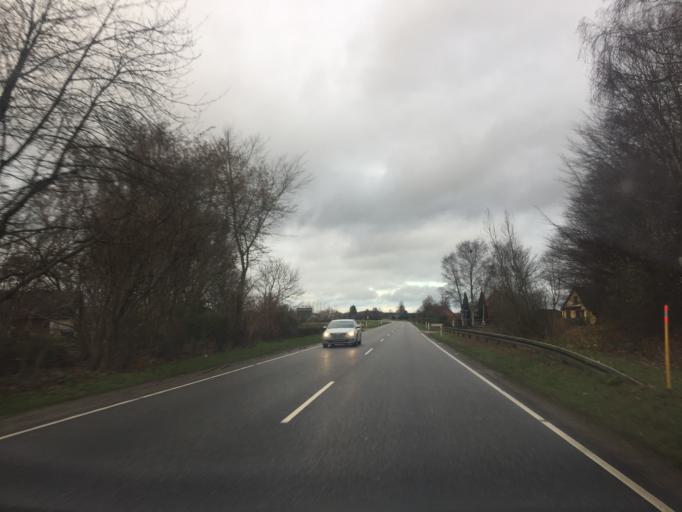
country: DK
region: Zealand
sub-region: Soro Kommune
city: Stenlille
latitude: 55.5768
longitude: 11.6498
